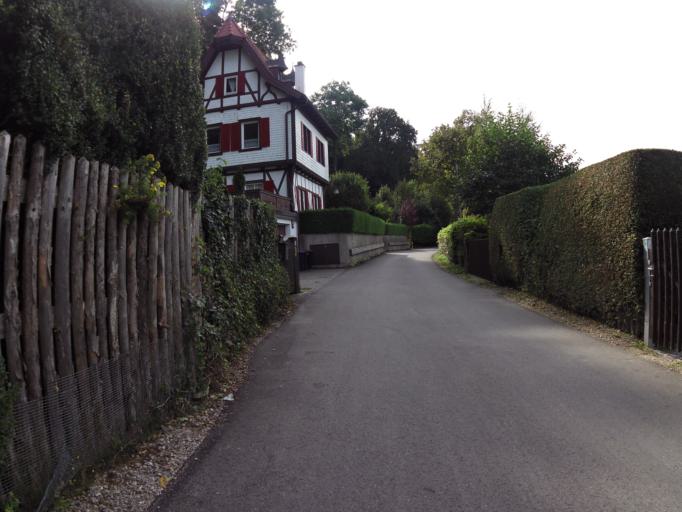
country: DE
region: Bavaria
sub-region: Upper Bavaria
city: Berg
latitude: 47.9487
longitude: 11.3419
